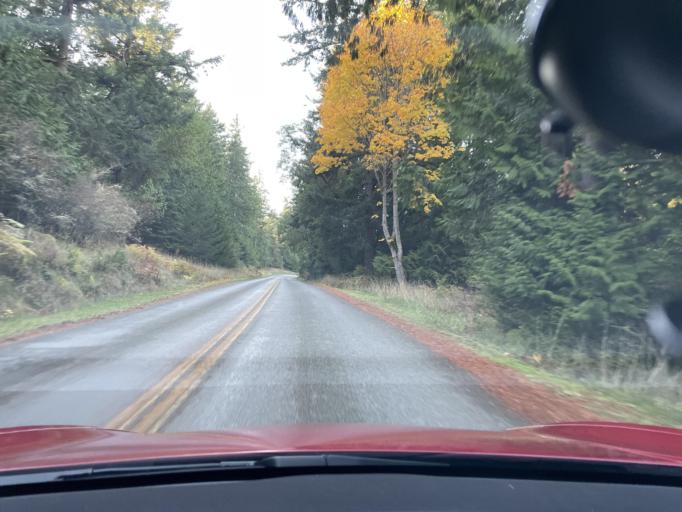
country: US
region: Washington
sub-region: San Juan County
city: Friday Harbor
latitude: 48.5292
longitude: -123.1517
